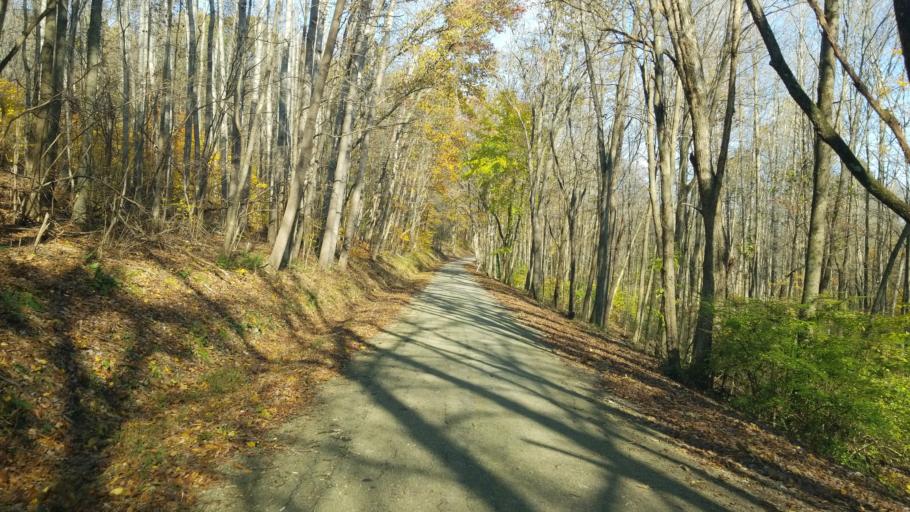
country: US
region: Ohio
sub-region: Sandusky County
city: Bellville
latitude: 40.6354
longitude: -82.4733
